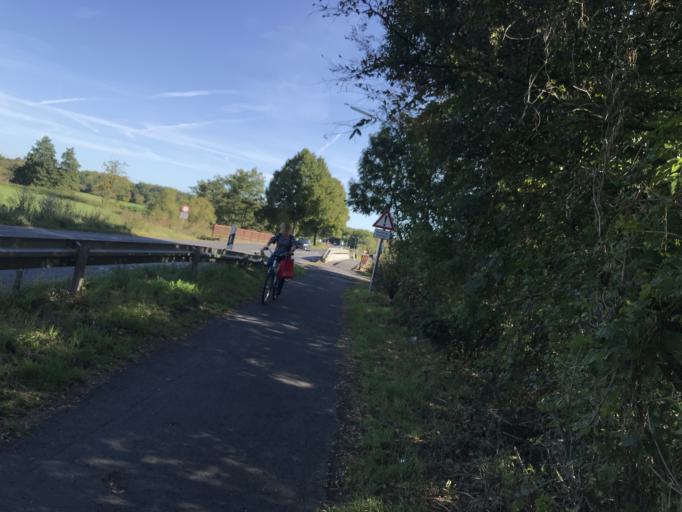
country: DE
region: Hesse
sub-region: Regierungsbezirk Darmstadt
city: Altenstadt
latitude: 50.2783
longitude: 8.9472
